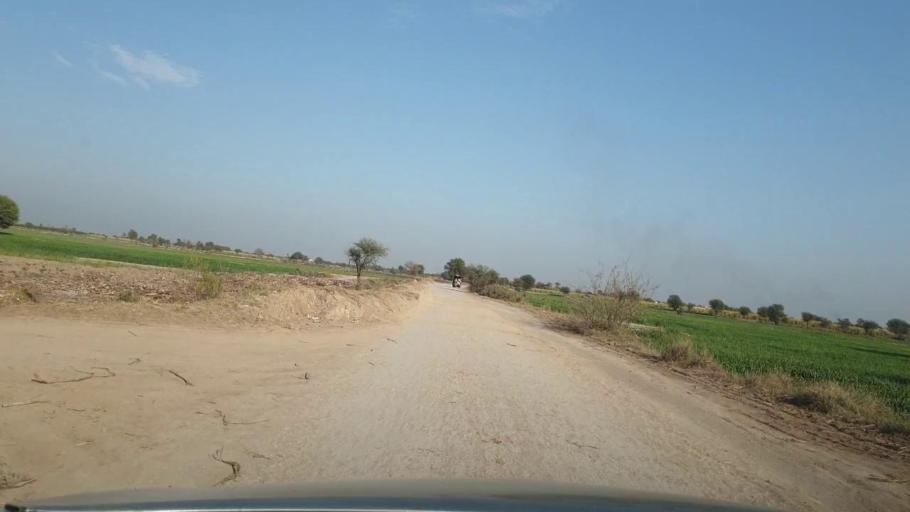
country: PK
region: Sindh
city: Tando Allahyar
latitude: 25.5934
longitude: 68.6677
